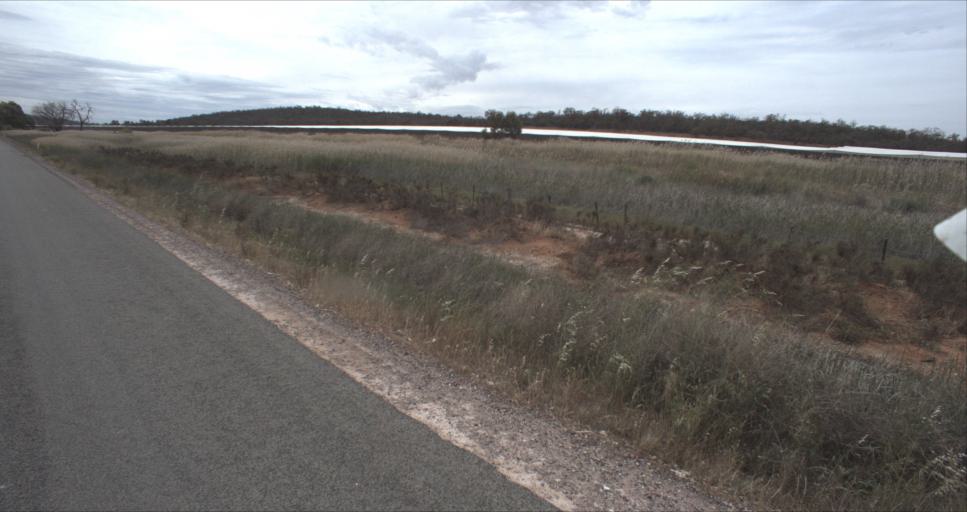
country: AU
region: New South Wales
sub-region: Leeton
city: Leeton
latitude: -34.4327
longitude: 146.3769
